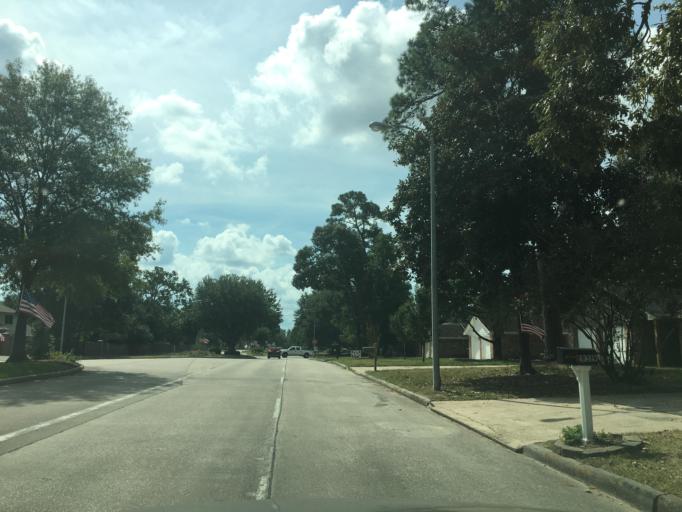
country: US
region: Texas
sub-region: Harris County
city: Spring
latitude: 30.1160
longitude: -95.3957
